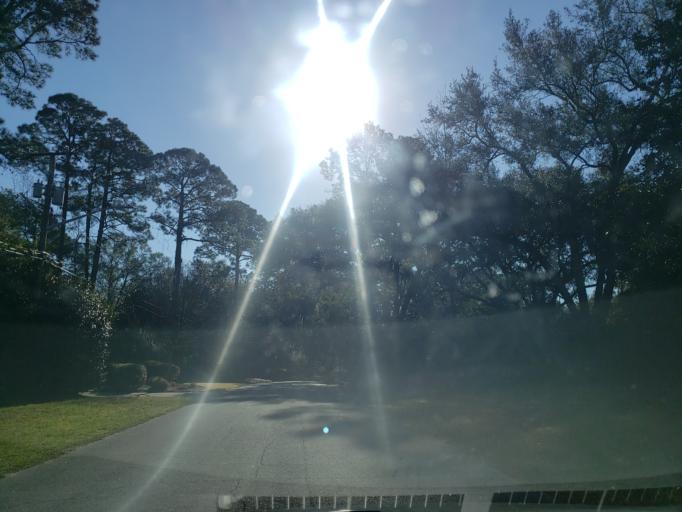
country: US
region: Georgia
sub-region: Chatham County
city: Thunderbolt
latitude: 32.0217
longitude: -81.0923
